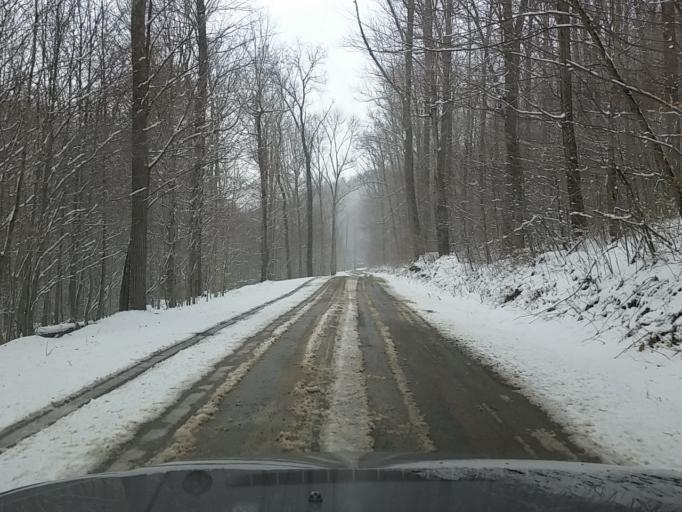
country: US
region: Pennsylvania
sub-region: Sullivan County
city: Laporte
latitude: 41.3309
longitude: -76.4612
